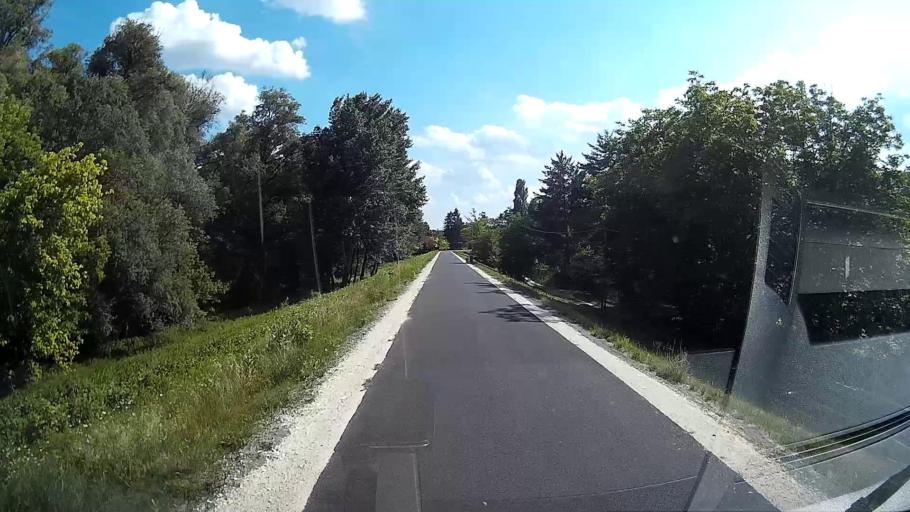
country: HU
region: Pest
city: God
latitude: 47.6685
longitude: 19.1128
